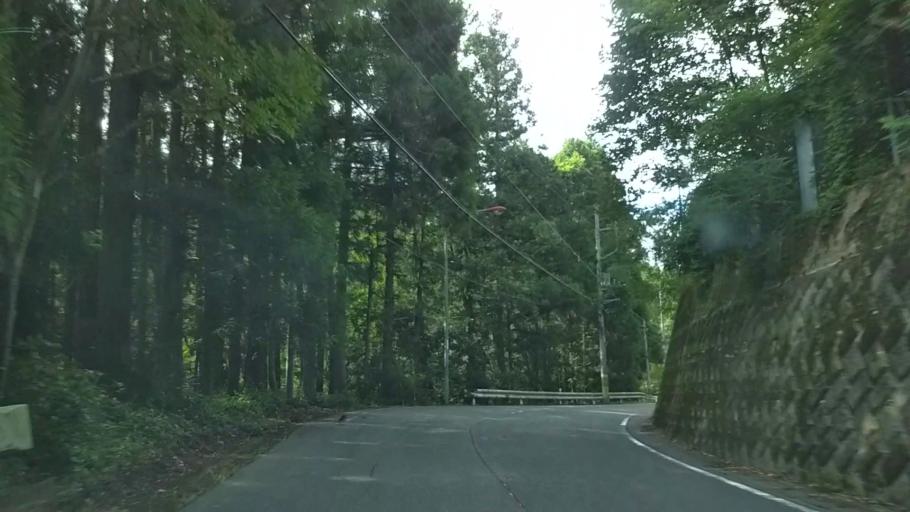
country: JP
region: Yamanashi
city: Uenohara
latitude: 35.5792
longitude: 139.1507
